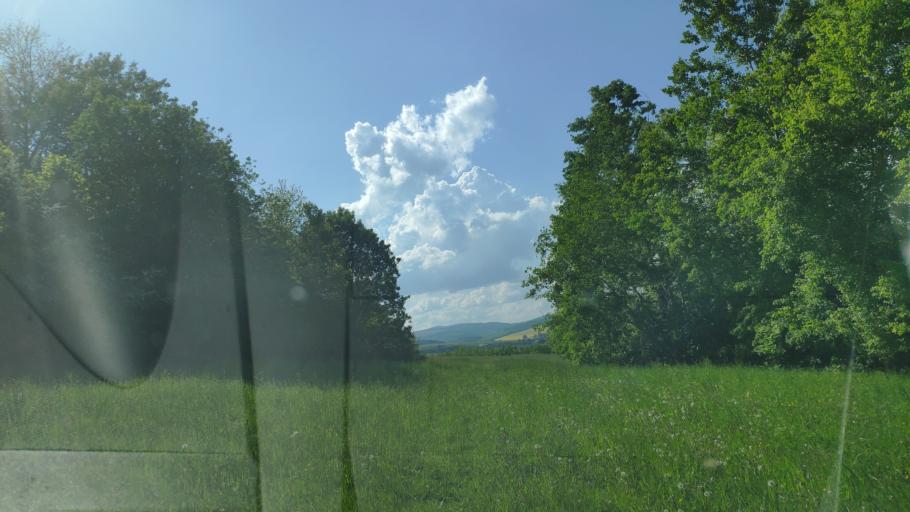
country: SK
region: Presovsky
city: Sabinov
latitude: 49.0527
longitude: 21.1499
